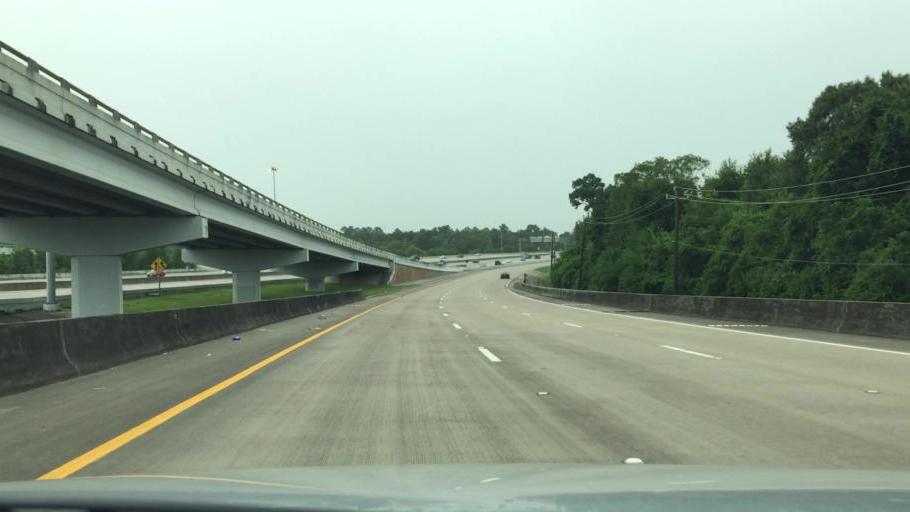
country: US
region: Texas
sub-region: Harris County
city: Cloverleaf
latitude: 29.7756
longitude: -95.1567
